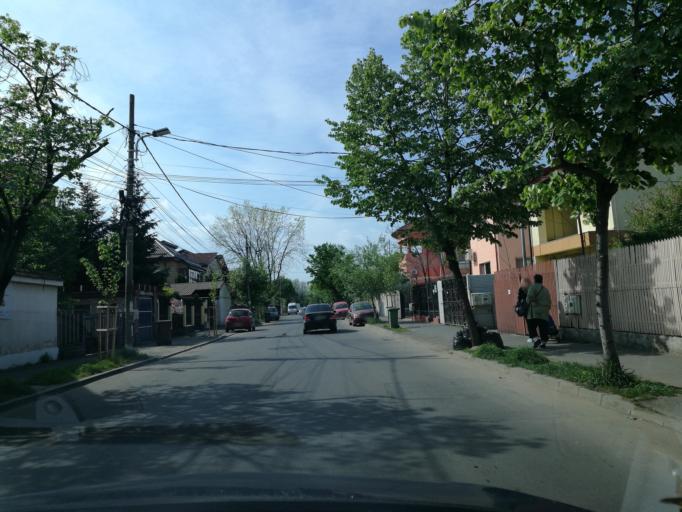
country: RO
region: Ilfov
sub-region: Comuna Chiajna
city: Rosu
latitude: 44.4421
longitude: 26.0306
